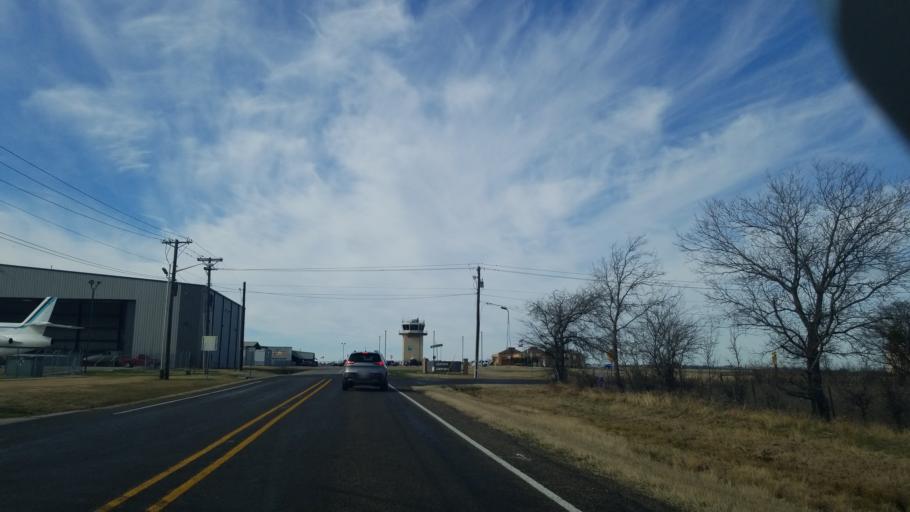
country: US
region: Texas
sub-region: Denton County
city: Denton
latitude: 33.2020
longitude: -97.1920
